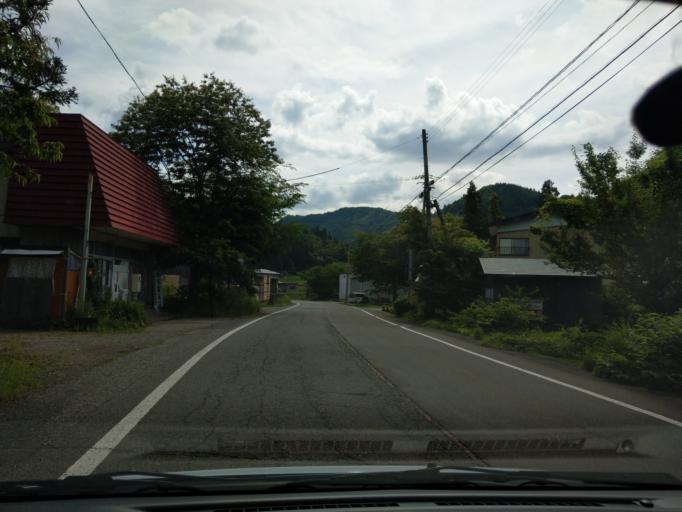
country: JP
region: Akita
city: Kakunodatemachi
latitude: 39.7461
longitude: 140.5951
